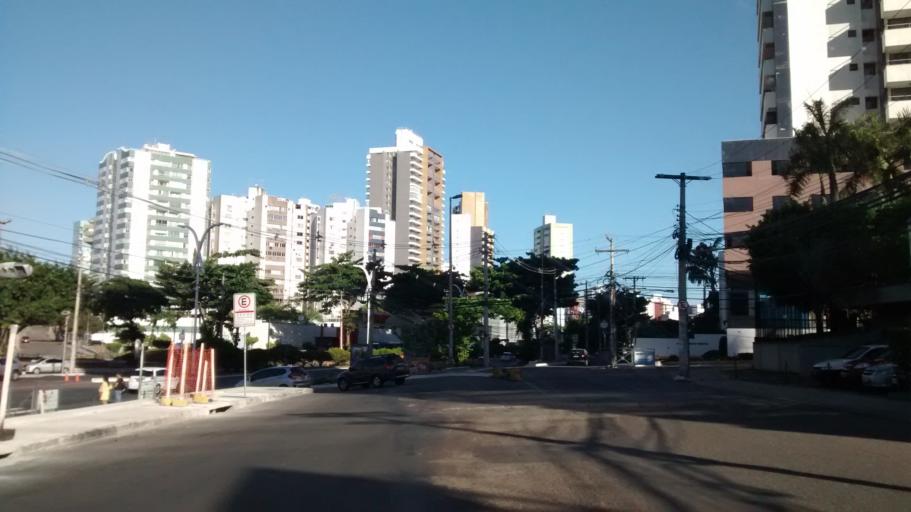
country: BR
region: Bahia
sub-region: Salvador
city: Salvador
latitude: -12.9973
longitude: -38.4646
